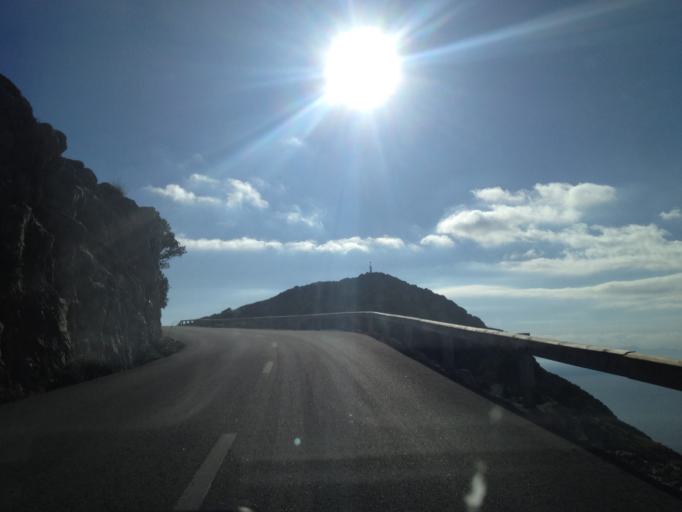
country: ES
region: Balearic Islands
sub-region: Illes Balears
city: Alcudia
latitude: 39.9575
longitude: 3.2091
